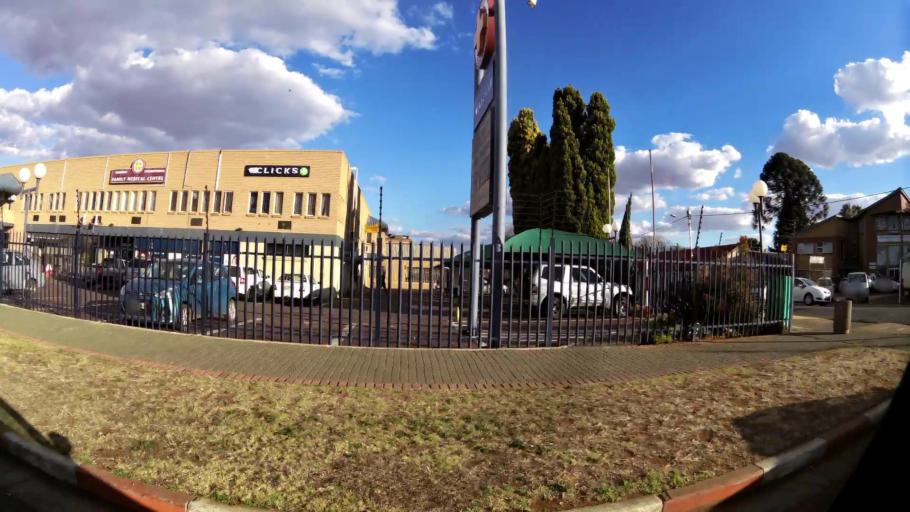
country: ZA
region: North-West
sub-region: Dr Kenneth Kaunda District Municipality
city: Potchefstroom
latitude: -26.7107
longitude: 27.0935
